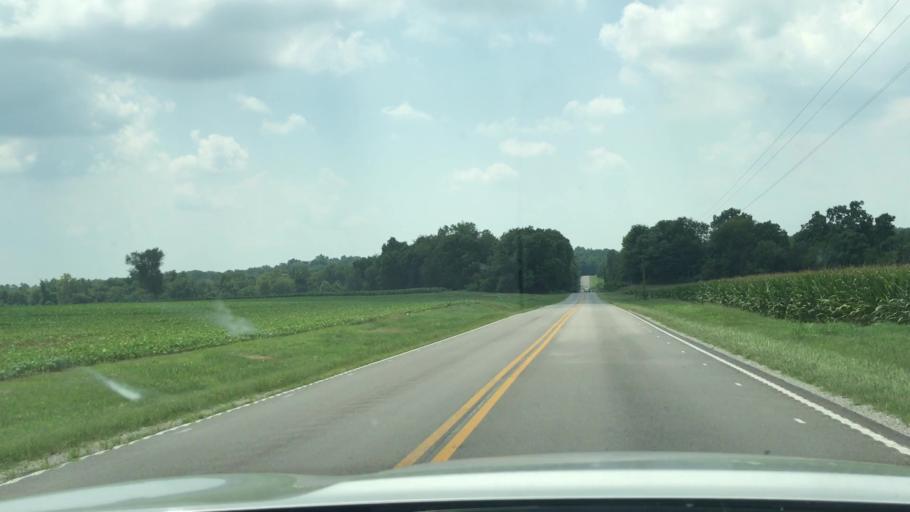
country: US
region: Kentucky
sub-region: Todd County
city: Guthrie
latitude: 36.7159
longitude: -87.0961
